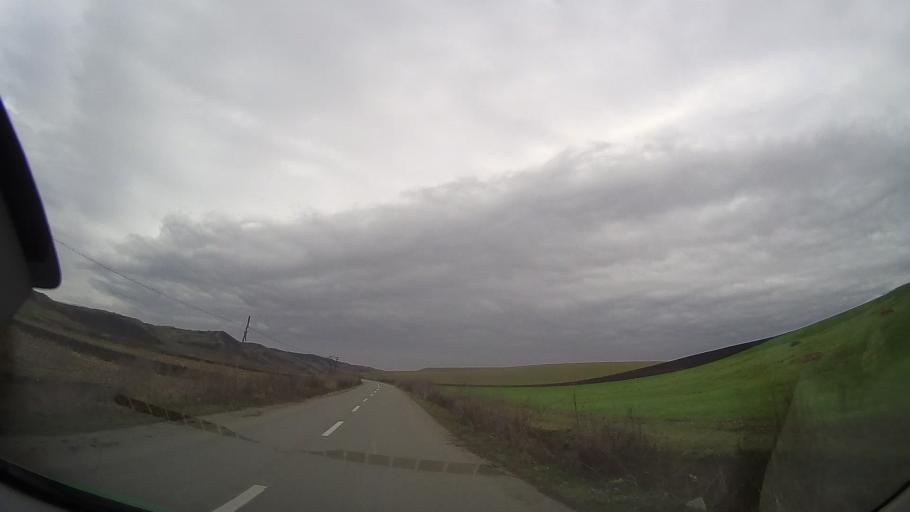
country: RO
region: Bistrita-Nasaud
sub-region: Comuna Milas
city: Milas
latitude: 46.7897
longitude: 24.4219
